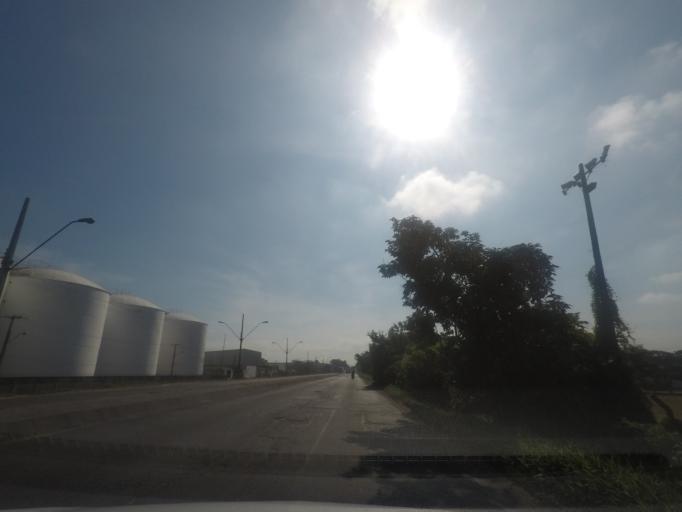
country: BR
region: Parana
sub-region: Paranagua
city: Paranagua
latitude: -25.5198
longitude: -48.5248
